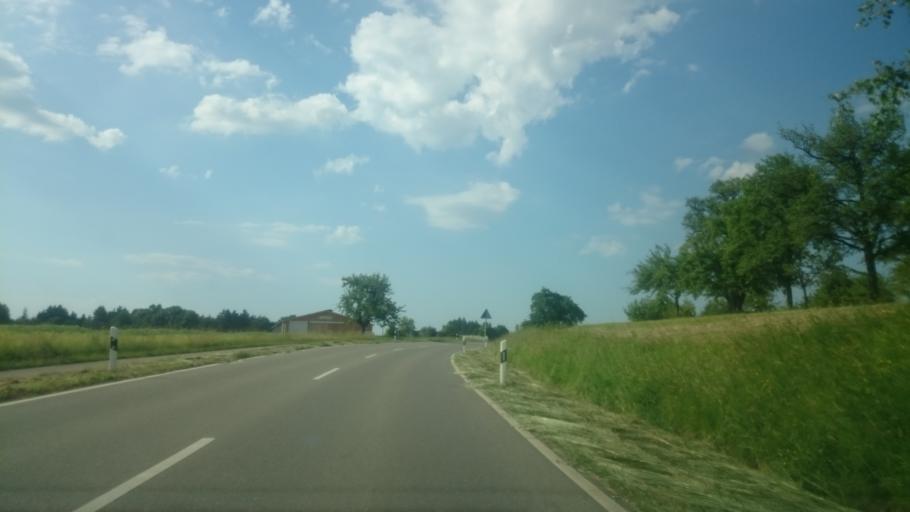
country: DE
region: Baden-Wuerttemberg
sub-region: Tuebingen Region
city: Gomaringen
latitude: 48.4192
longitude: 9.1105
